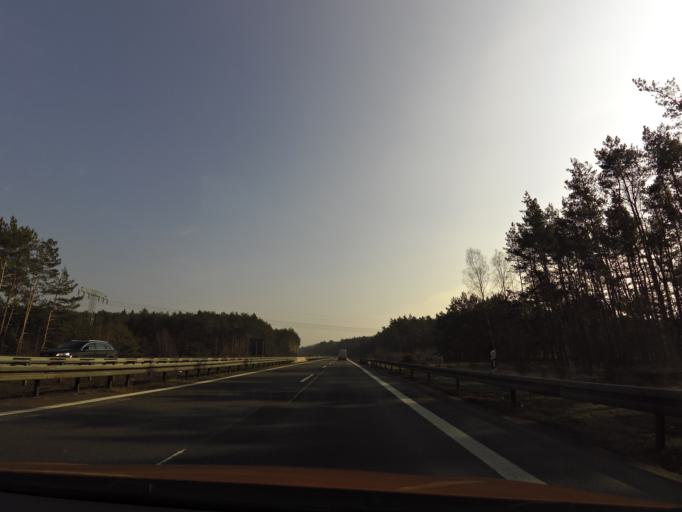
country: DE
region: Brandenburg
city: Storkow
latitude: 52.3141
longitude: 13.9162
